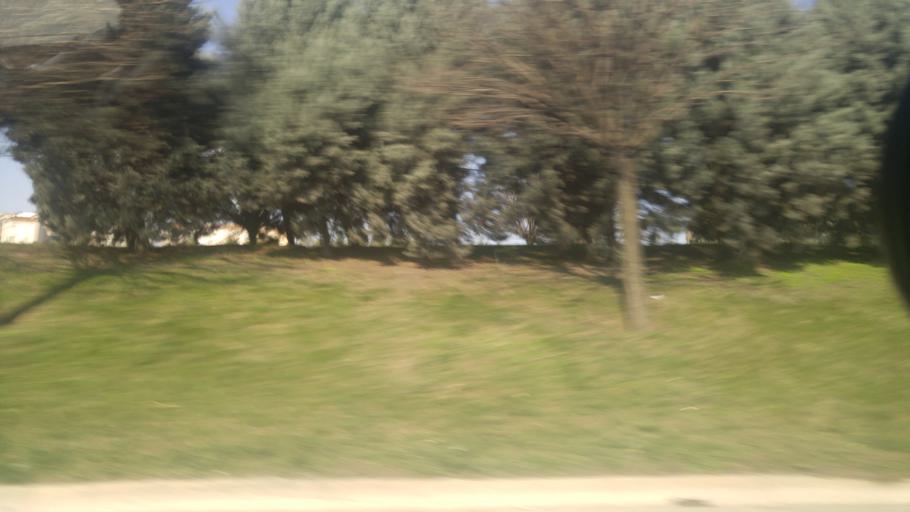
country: TR
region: Kocaeli
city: Balcik
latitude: 40.8622
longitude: 29.3819
